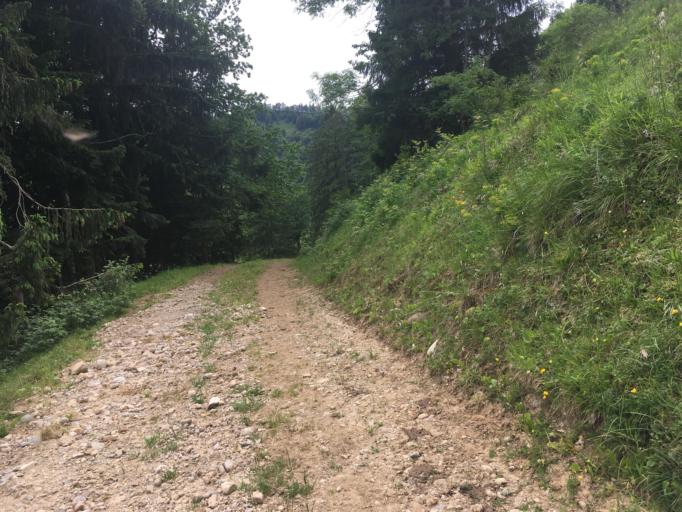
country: CH
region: Saint Gallen
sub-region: Wahlkreis Toggenburg
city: Lichtensteig
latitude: 47.3195
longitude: 9.0466
